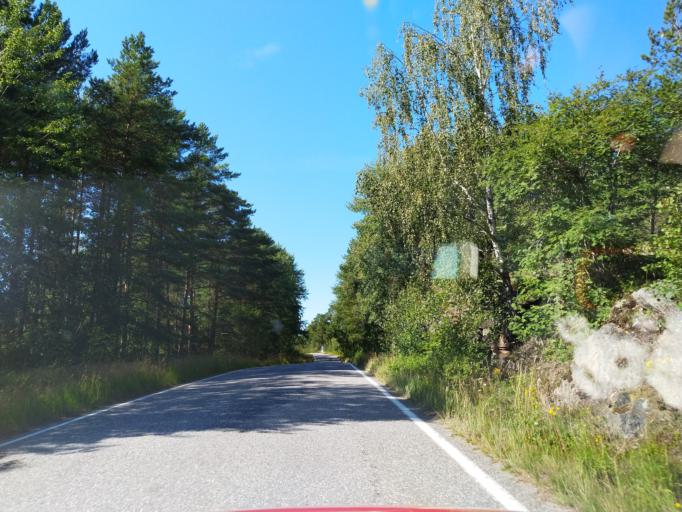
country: FI
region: Varsinais-Suomi
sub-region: Aboland-Turunmaa
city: Dragsfjaerd
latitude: 60.0277
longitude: 22.4648
